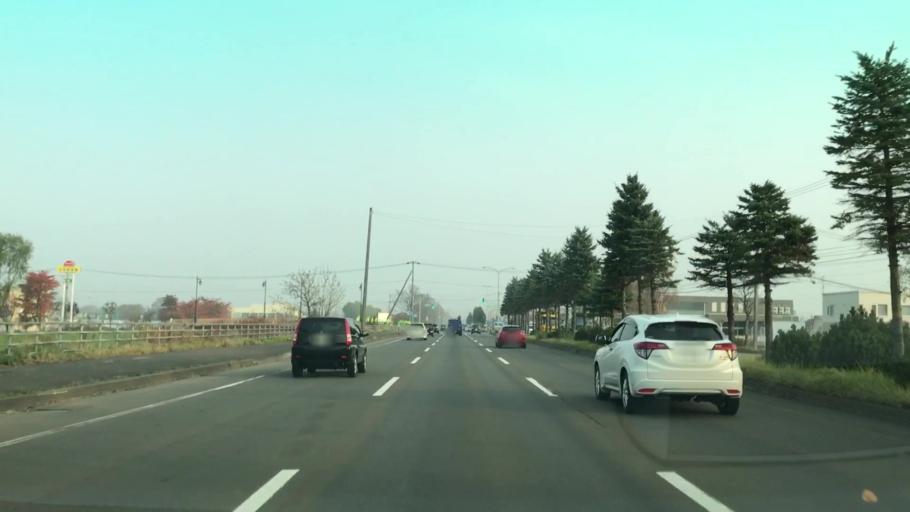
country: JP
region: Hokkaido
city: Sapporo
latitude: 43.1488
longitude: 141.3506
